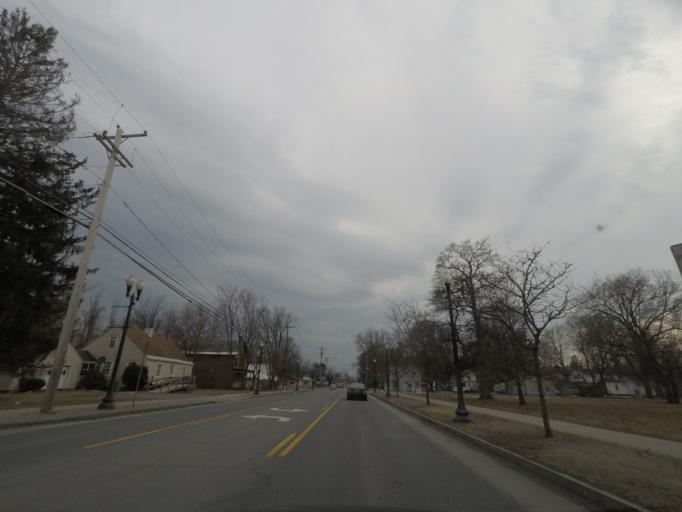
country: US
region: New York
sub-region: Washington County
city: Fort Edward
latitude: 43.2808
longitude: -73.5865
